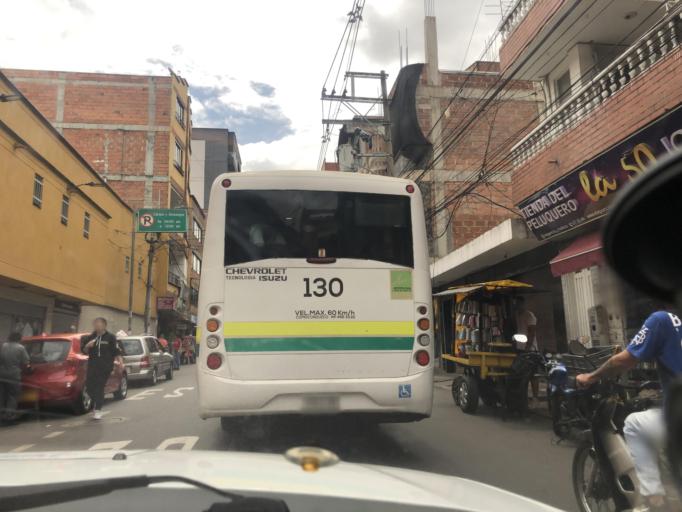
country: CO
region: Antioquia
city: Bello
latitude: 6.3387
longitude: -75.5591
